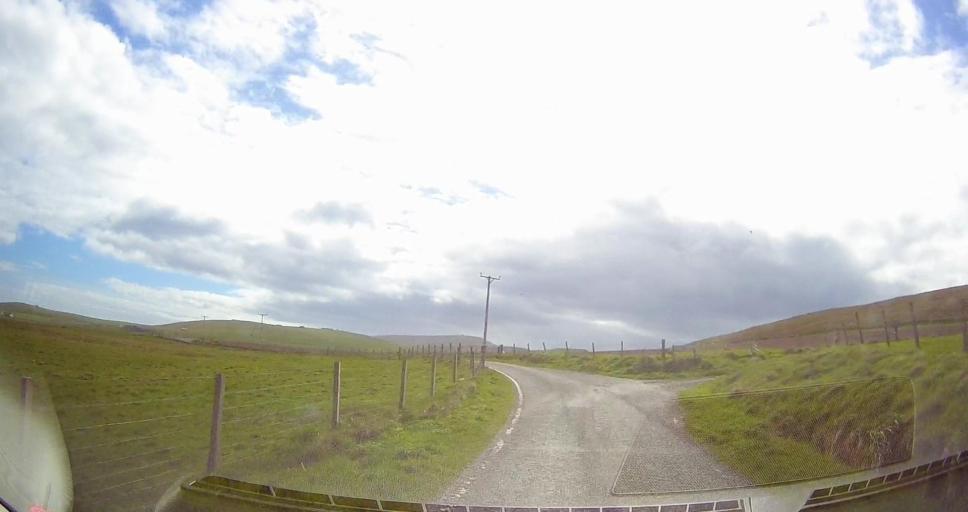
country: GB
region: Scotland
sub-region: Shetland Islands
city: Sandwick
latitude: 59.9409
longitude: -1.3457
